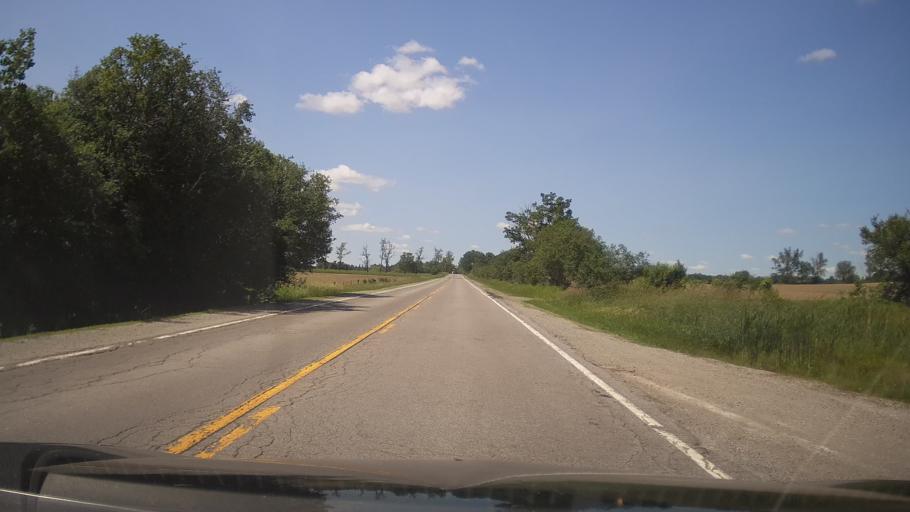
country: CA
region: Ontario
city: Oshawa
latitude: 43.9856
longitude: -78.8588
